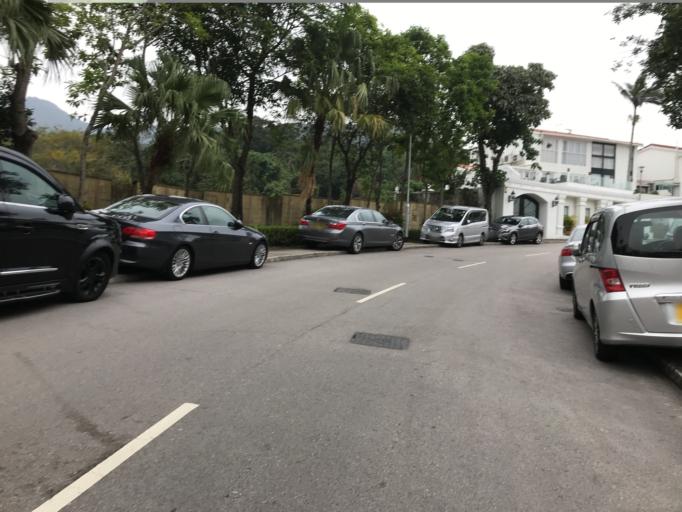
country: HK
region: Tai Po
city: Tai Po
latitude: 22.4659
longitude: 114.1549
